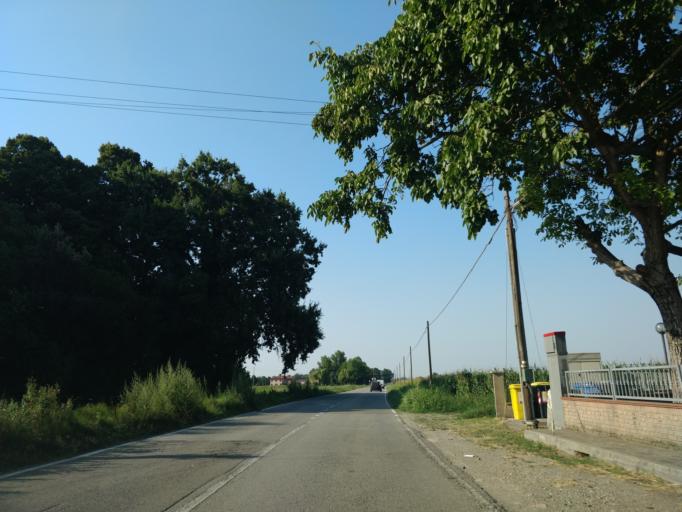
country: IT
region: Emilia-Romagna
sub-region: Provincia di Bologna
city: Argelato
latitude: 44.6103
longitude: 11.3350
